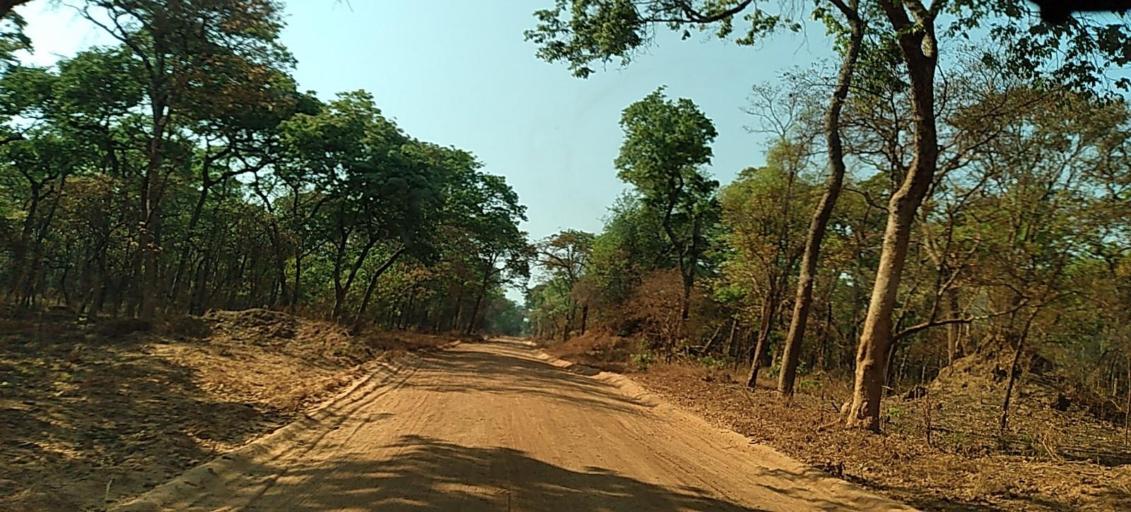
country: ZM
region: North-Western
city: Kasempa
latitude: -13.6760
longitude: 26.0202
